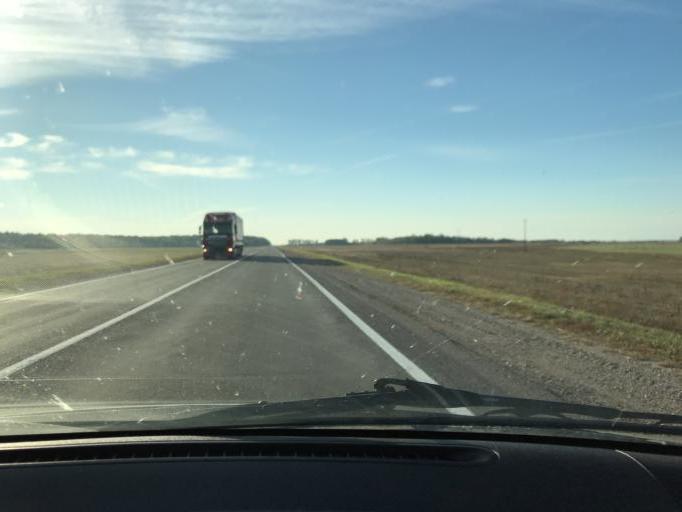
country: BY
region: Brest
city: Antopal'
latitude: 52.2273
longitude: 24.7836
